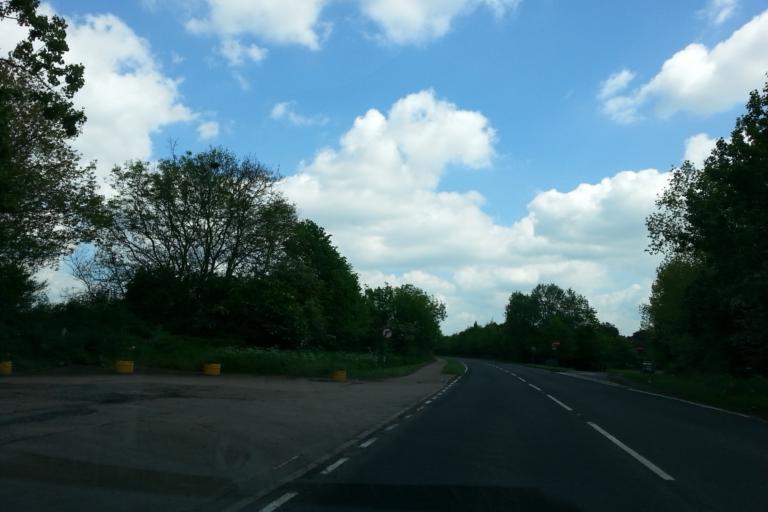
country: GB
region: England
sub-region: Cambridgeshire
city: Yaxley
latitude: 52.5116
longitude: -0.2743
